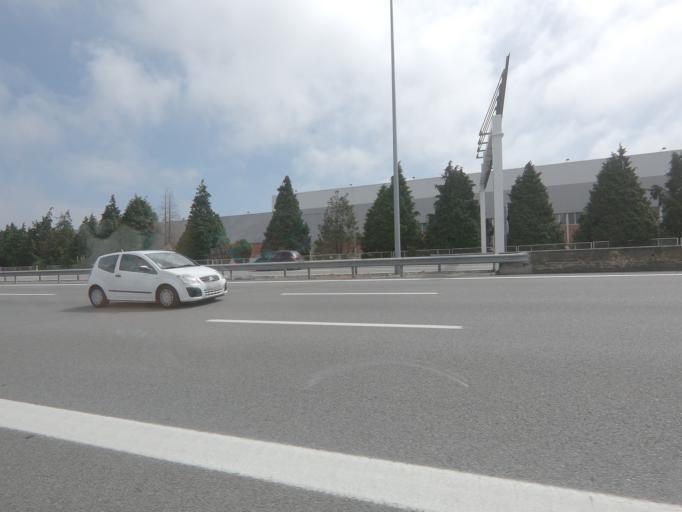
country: PT
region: Porto
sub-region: Matosinhos
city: Santa Cruz do Bispo
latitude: 41.2153
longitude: -8.6908
